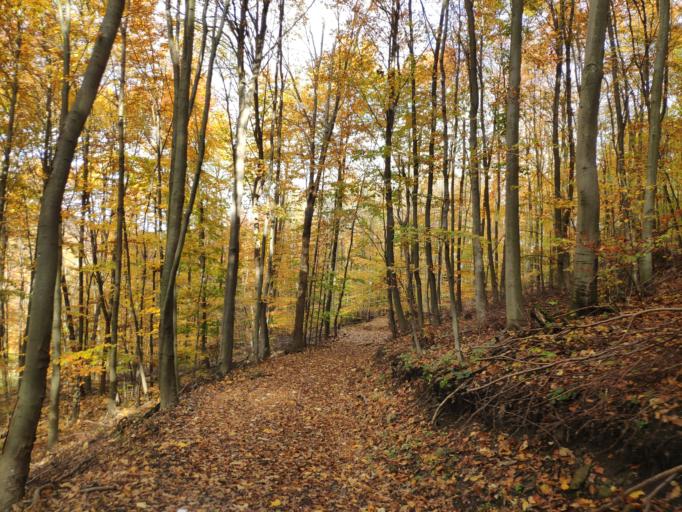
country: SK
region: Presovsky
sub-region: Okres Presov
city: Presov
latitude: 48.8545
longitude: 21.1884
